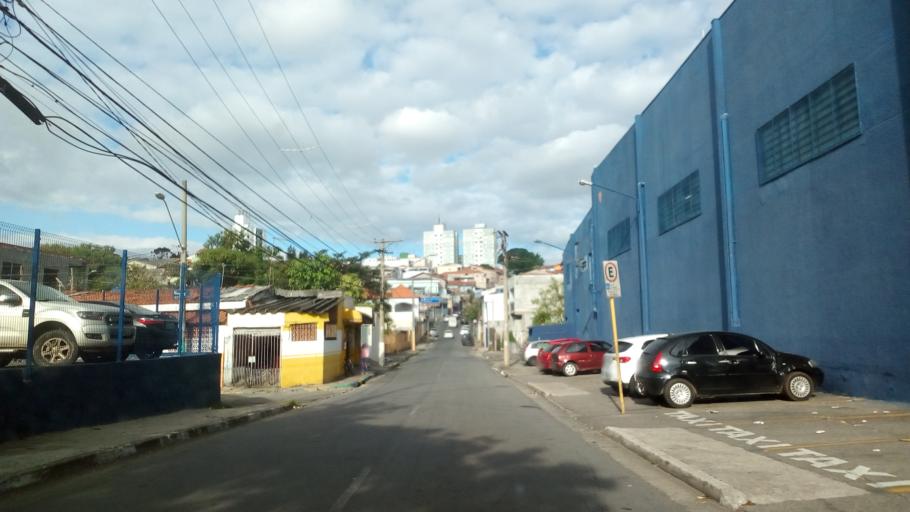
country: BR
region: Sao Paulo
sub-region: Guarulhos
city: Guarulhos
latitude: -23.4600
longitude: -46.5194
